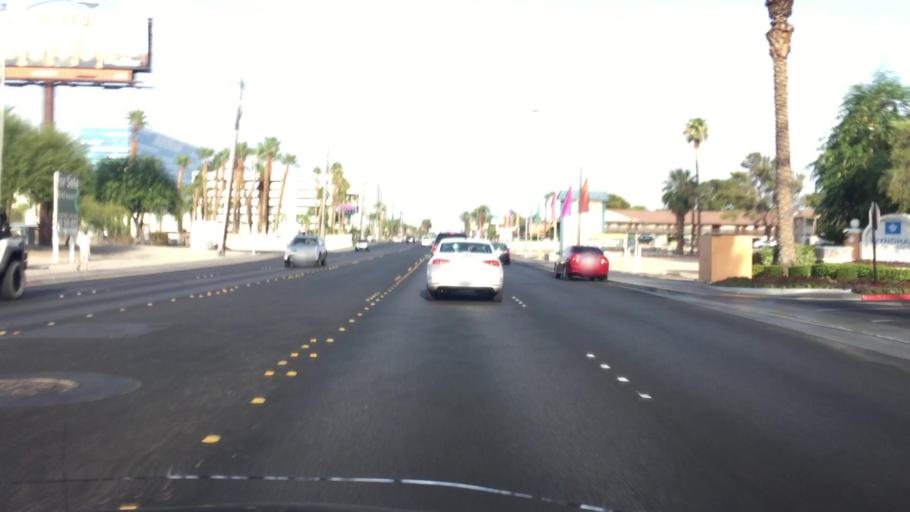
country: US
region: Nevada
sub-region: Clark County
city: Paradise
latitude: 36.1080
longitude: -115.1605
